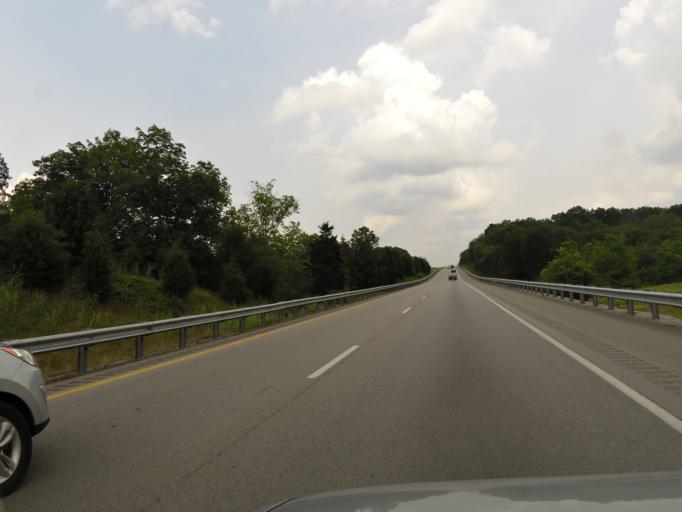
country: US
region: Indiana
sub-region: Switzerland County
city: Vevay
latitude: 38.6765
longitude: -84.9850
